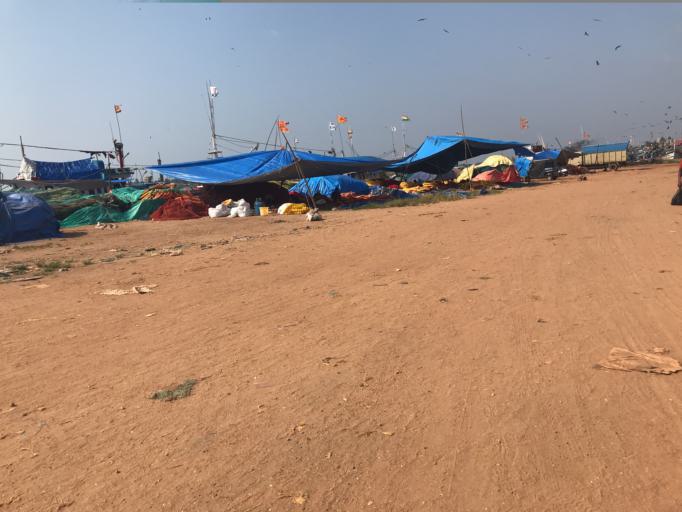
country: IN
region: Karnataka
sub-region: Dakshina Kannada
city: Ullal
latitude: 12.8515
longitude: 74.8332
